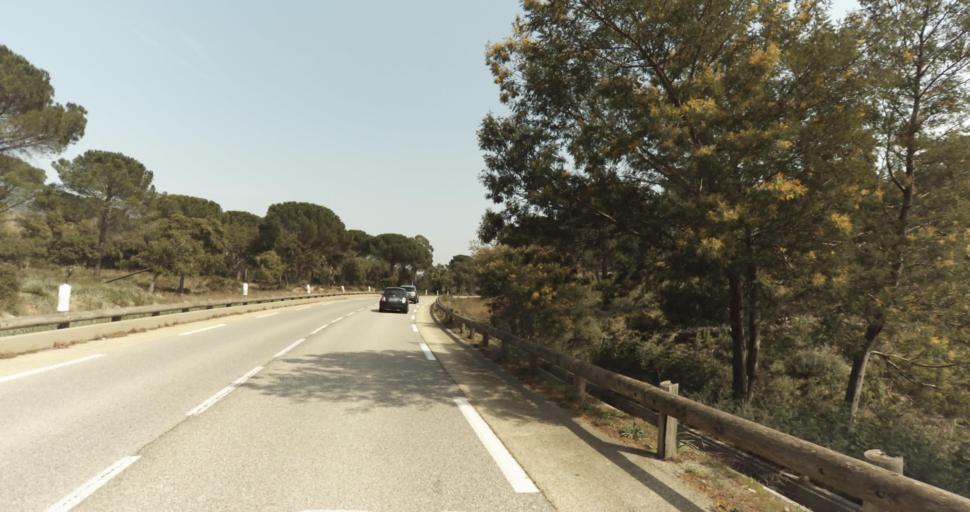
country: FR
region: Provence-Alpes-Cote d'Azur
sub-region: Departement du Var
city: Le Lavandou
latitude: 43.1902
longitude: 6.3701
